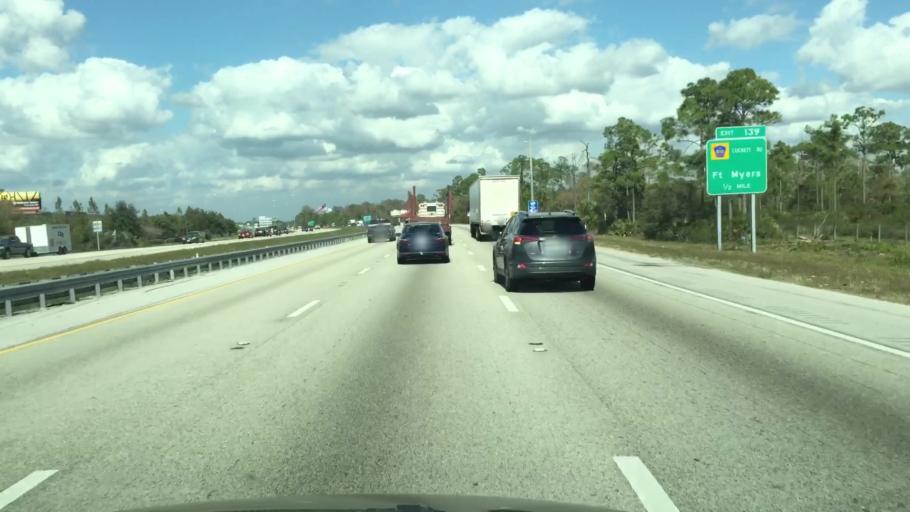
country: US
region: Florida
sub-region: Lee County
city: Tice
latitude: 26.6438
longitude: -81.7998
